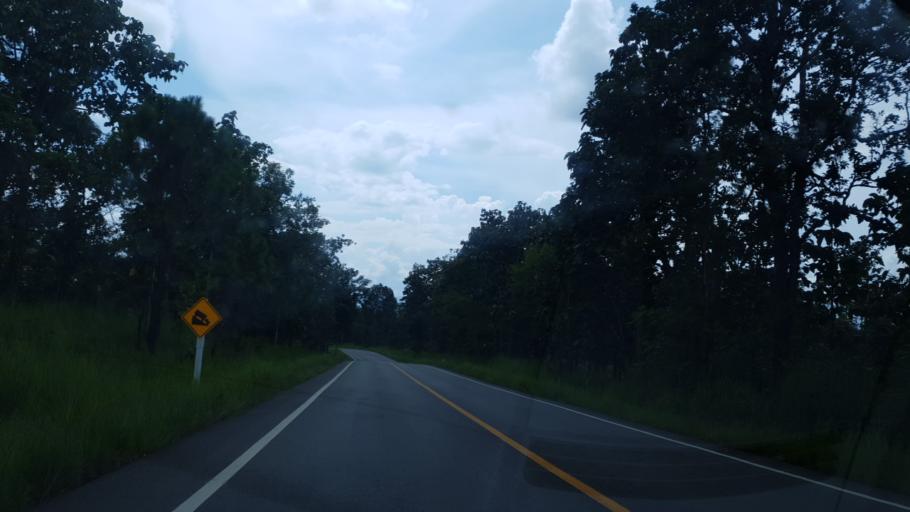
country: TH
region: Mae Hong Son
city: Khun Yuam
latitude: 18.7645
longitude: 97.9340
